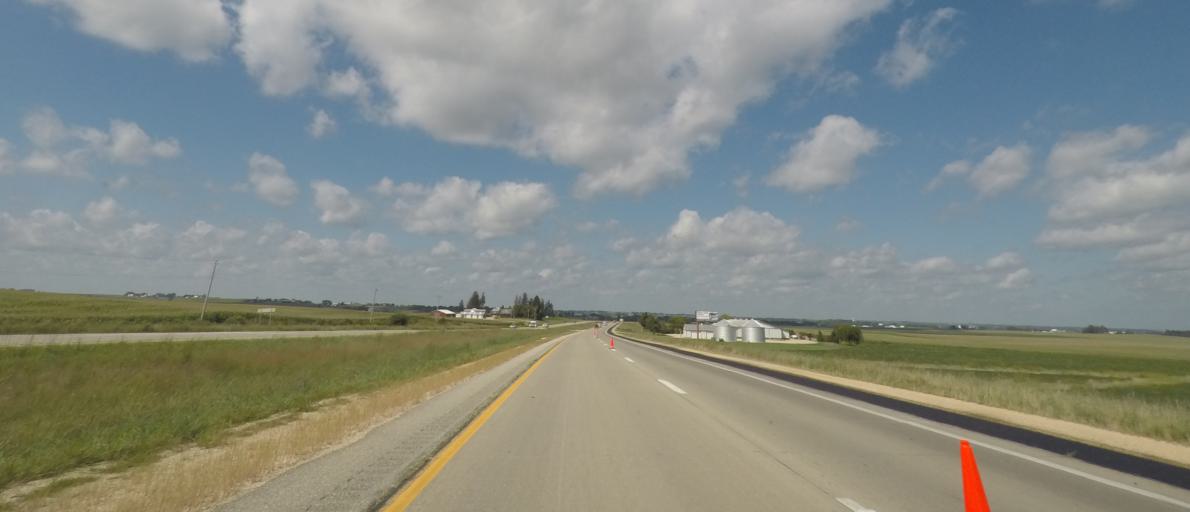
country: US
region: Iowa
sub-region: Jones County
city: Anamosa
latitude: 42.1669
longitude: -91.2289
